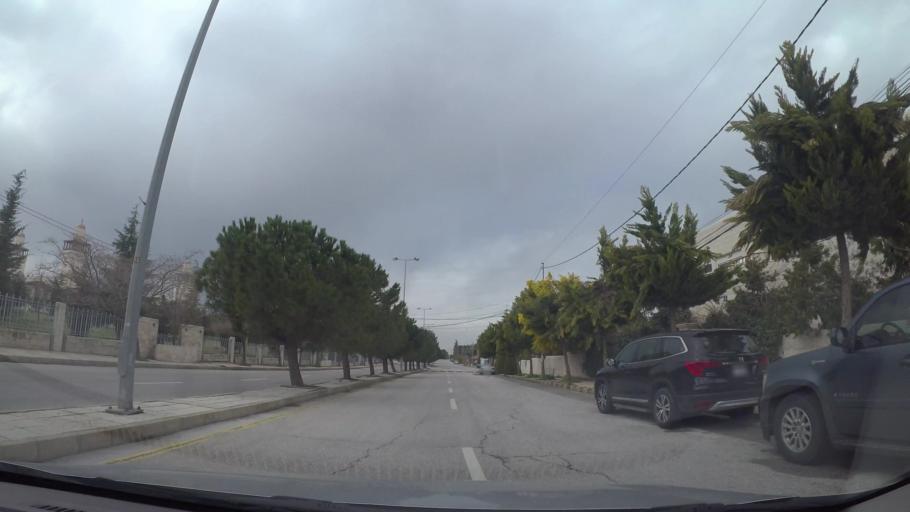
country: JO
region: Amman
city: Wadi as Sir
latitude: 31.9882
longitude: 35.8234
